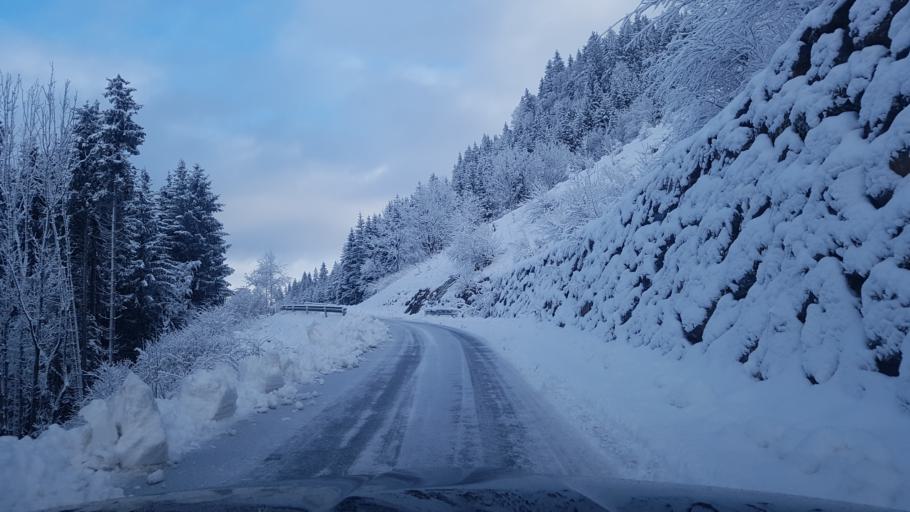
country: AT
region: Salzburg
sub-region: Politischer Bezirk Sankt Johann im Pongau
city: Sankt Johann im Pongau
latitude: 47.3210
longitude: 13.2041
